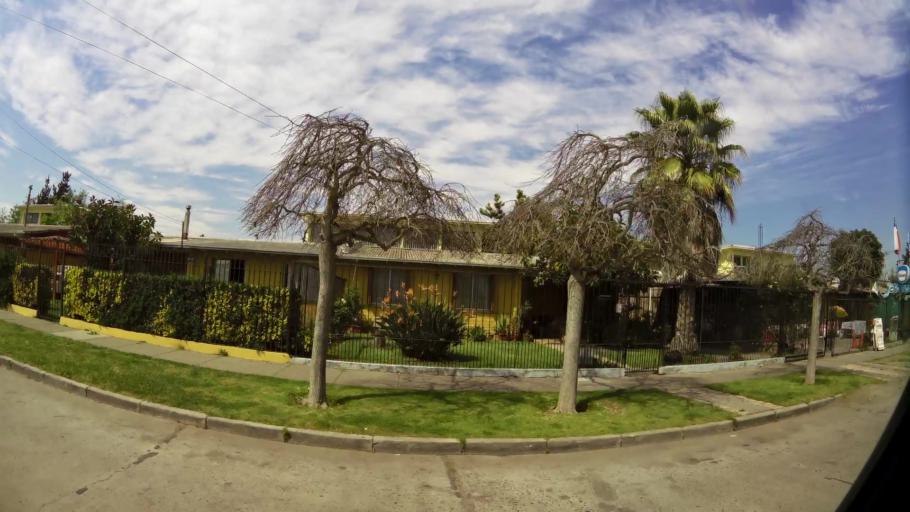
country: CL
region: Santiago Metropolitan
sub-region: Provincia de Talagante
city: Talagante
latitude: -33.6647
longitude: -70.9228
